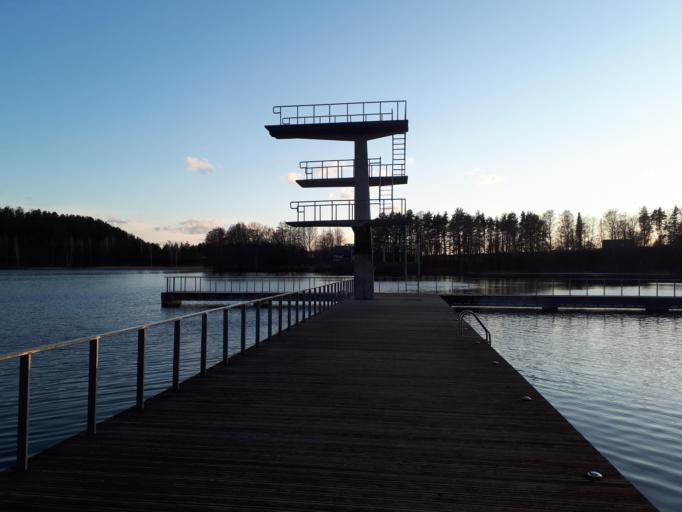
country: LT
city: Zarasai
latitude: 55.7274
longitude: 26.2506
